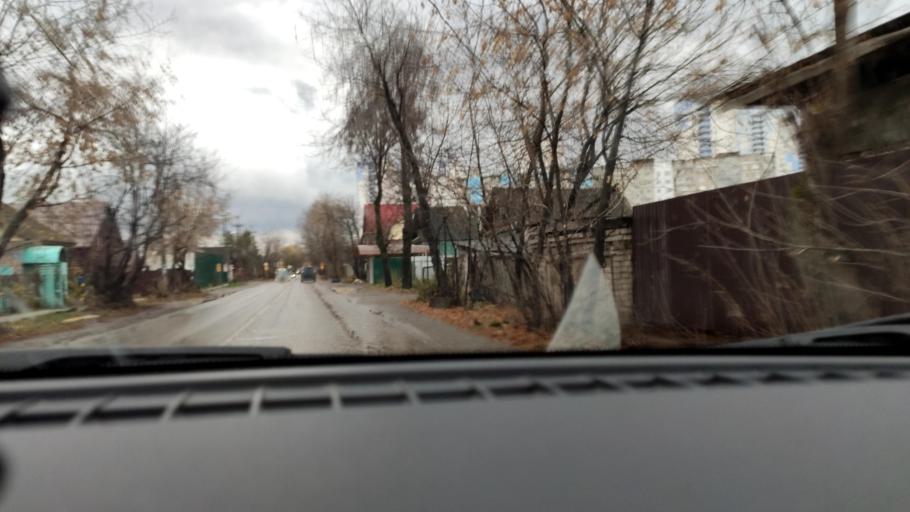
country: RU
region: Perm
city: Perm
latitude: 58.0099
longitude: 56.3218
